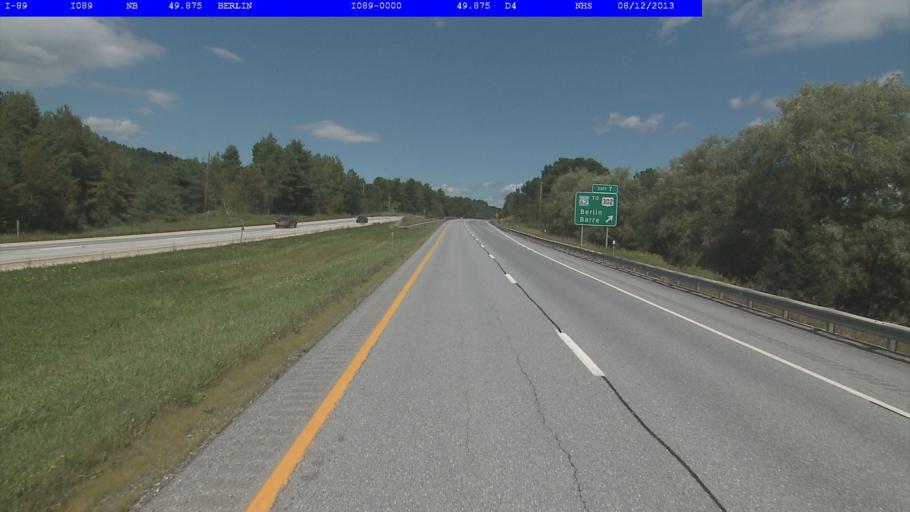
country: US
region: Vermont
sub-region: Washington County
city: Montpelier
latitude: 44.2098
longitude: -72.5818
